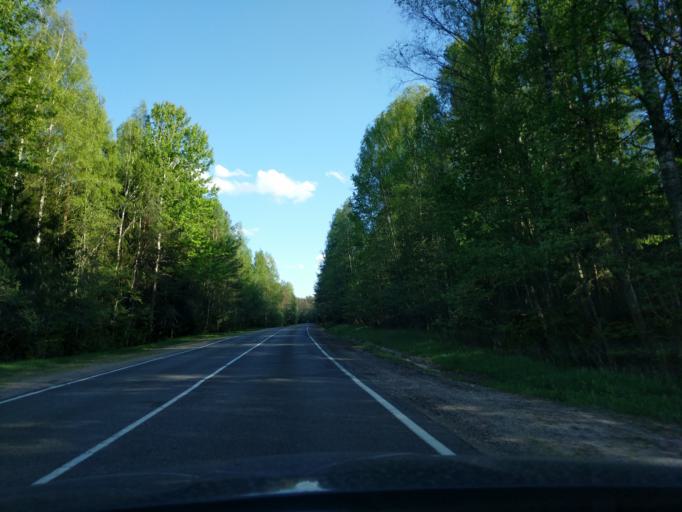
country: BY
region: Minsk
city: Myadzyel
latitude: 54.7855
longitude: 27.0357
